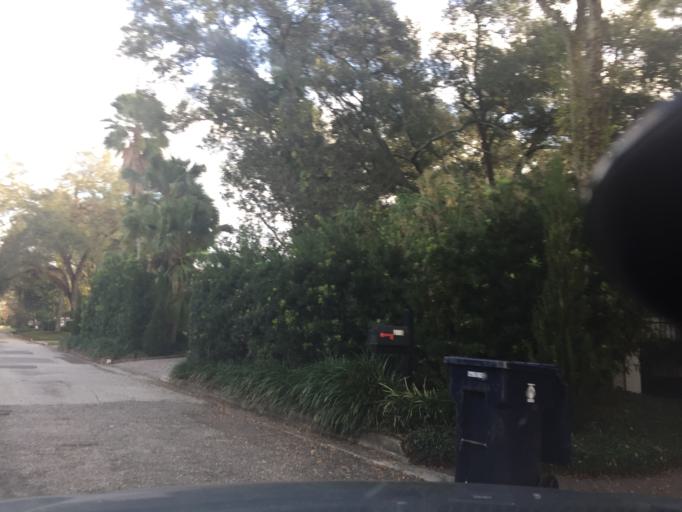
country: US
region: Florida
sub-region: Hillsborough County
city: Tampa
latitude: 27.9333
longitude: -82.4947
